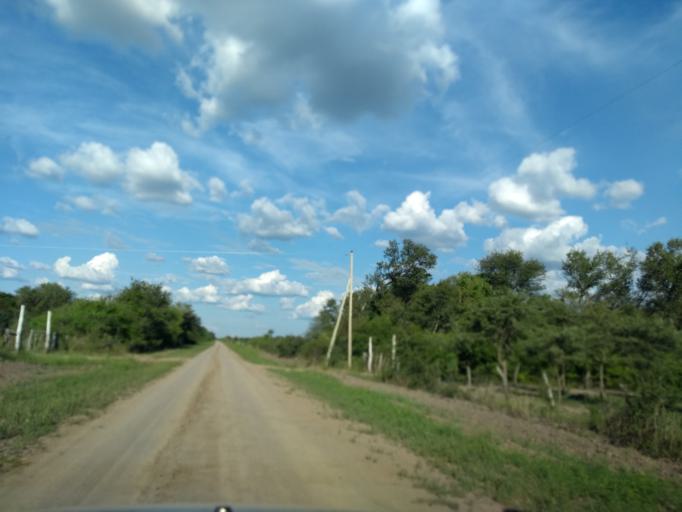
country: AR
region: Chaco
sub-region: Departamento de Quitilipi
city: Quitilipi
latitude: -26.7734
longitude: -60.1967
